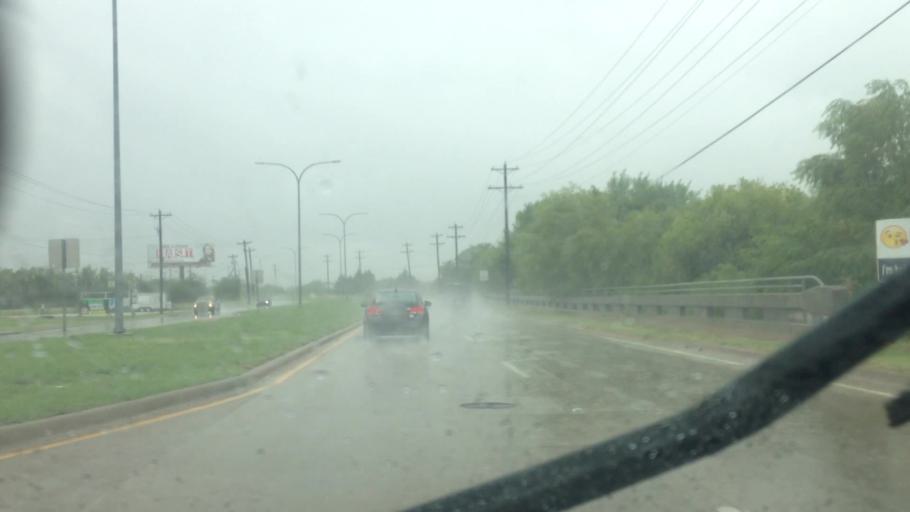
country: US
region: Texas
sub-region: Tarrant County
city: Keller
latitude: 32.9319
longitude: -97.2982
